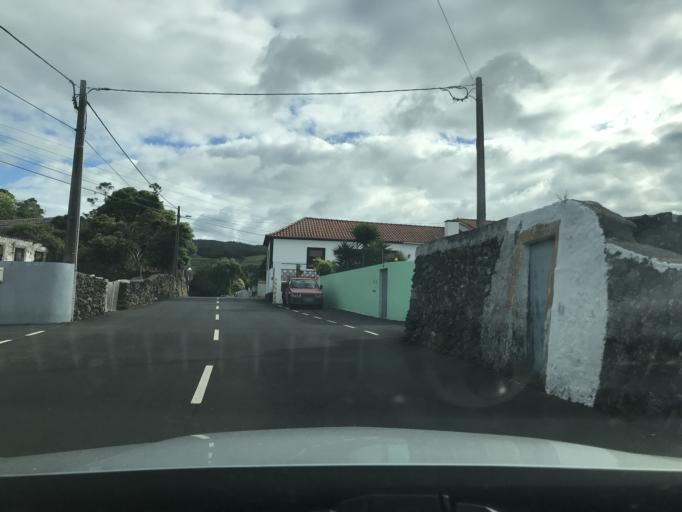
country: PT
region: Azores
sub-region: Angra do Heroismo
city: Angra do Heroismo
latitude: 38.6668
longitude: -27.2524
